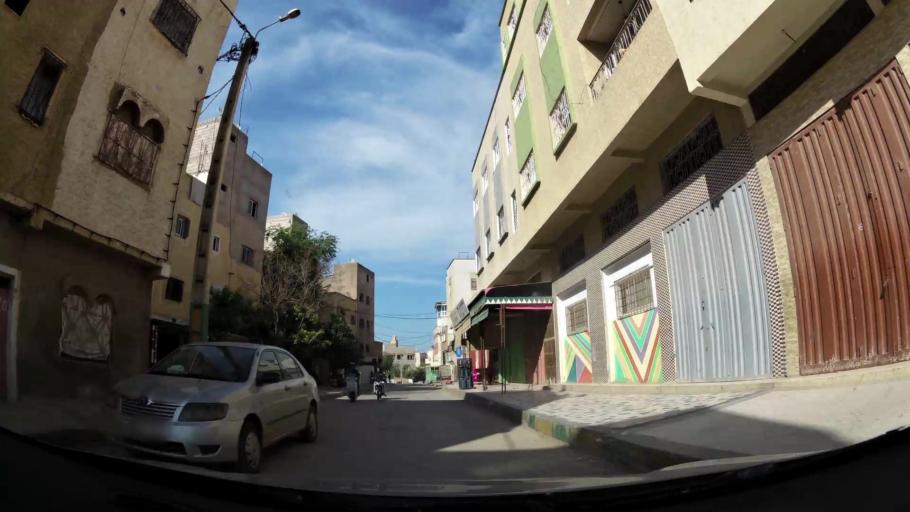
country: MA
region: Fes-Boulemane
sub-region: Fes
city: Fes
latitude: 34.0156
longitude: -5.0315
